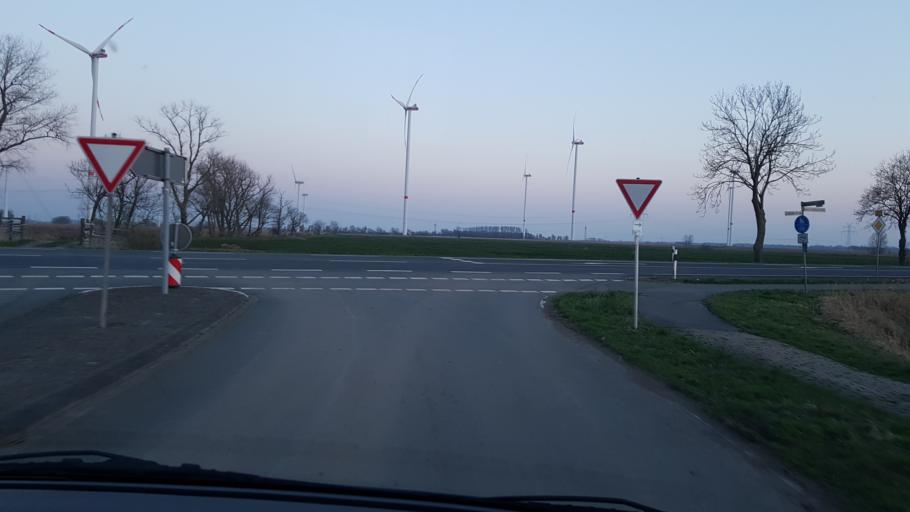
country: DE
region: Lower Saxony
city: Ovelgonne
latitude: 53.2813
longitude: 8.3692
